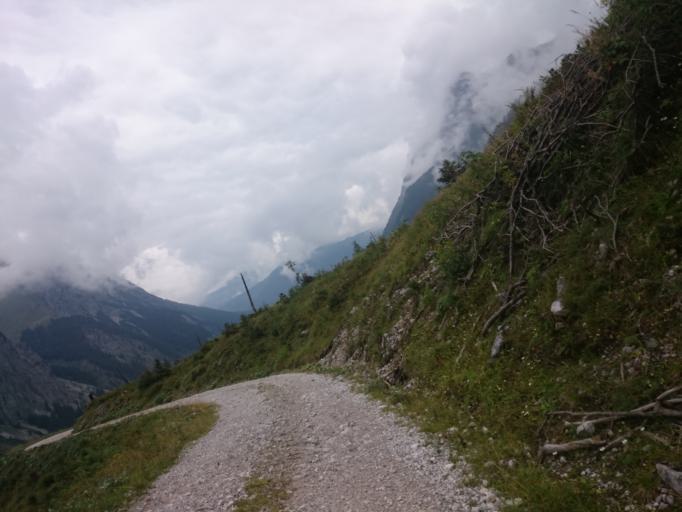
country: AT
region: Tyrol
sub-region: Politischer Bezirk Innsbruck Land
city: Absam
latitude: 47.4120
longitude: 11.4854
